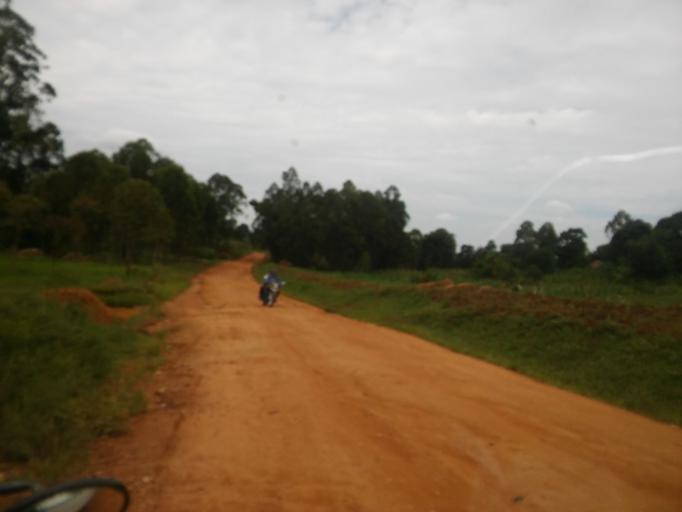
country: UG
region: Eastern Region
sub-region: Mbale District
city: Mbale
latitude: 0.9752
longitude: 34.2054
